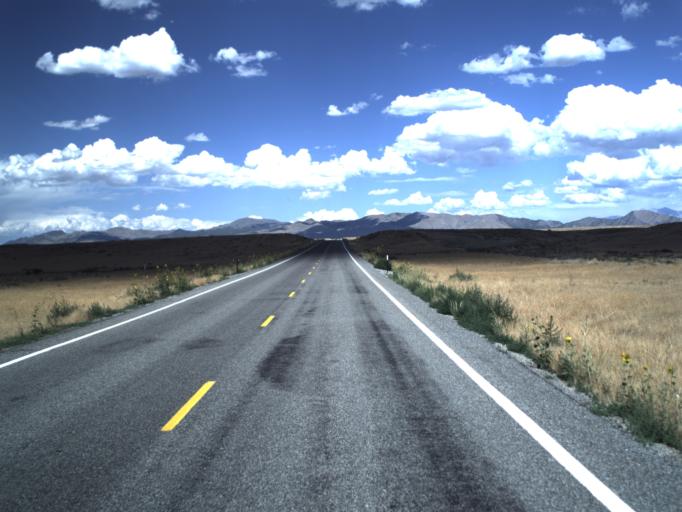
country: US
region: Utah
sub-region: Juab County
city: Nephi
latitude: 39.6803
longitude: -112.2522
